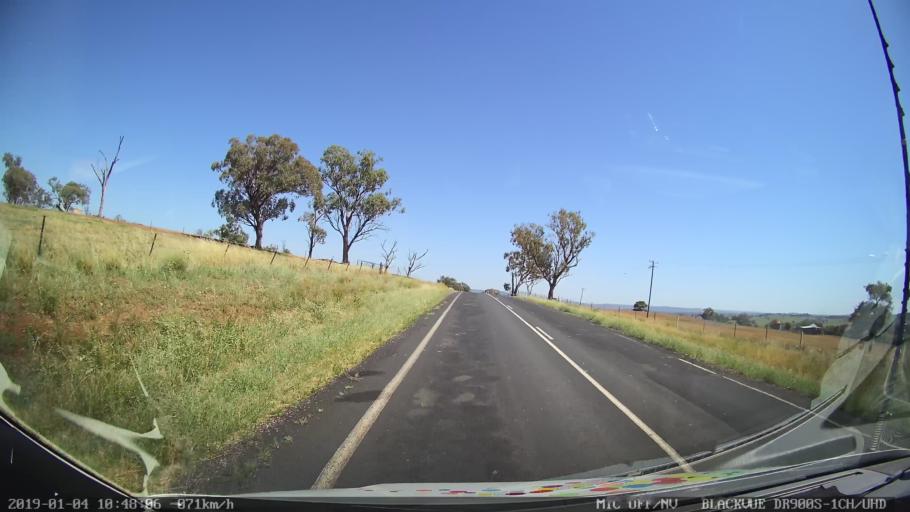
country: AU
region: New South Wales
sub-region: Cabonne
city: Molong
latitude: -33.2635
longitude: 148.7152
